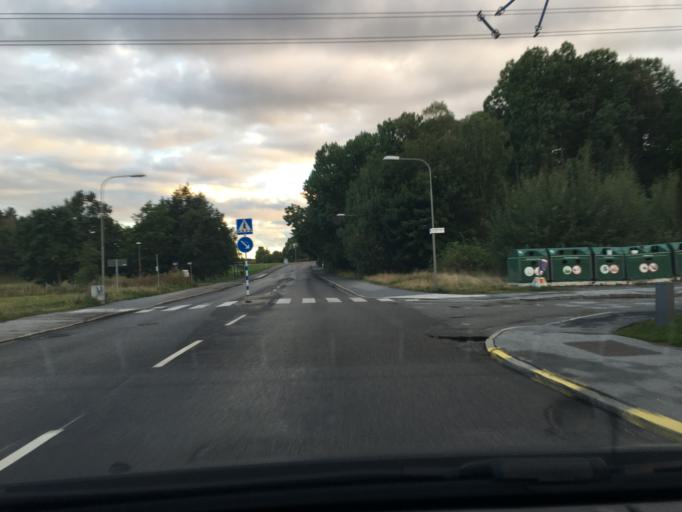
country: SE
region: Stockholm
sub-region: Jarfalla Kommun
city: Jakobsberg
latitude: 59.3742
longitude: 17.8698
